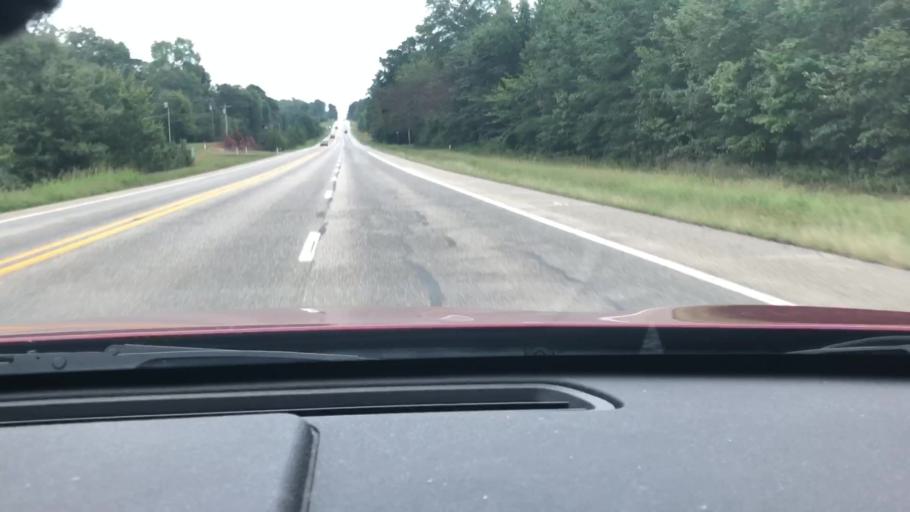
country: US
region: Arkansas
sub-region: Miller County
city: Texarkana
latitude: 33.4296
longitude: -93.9507
